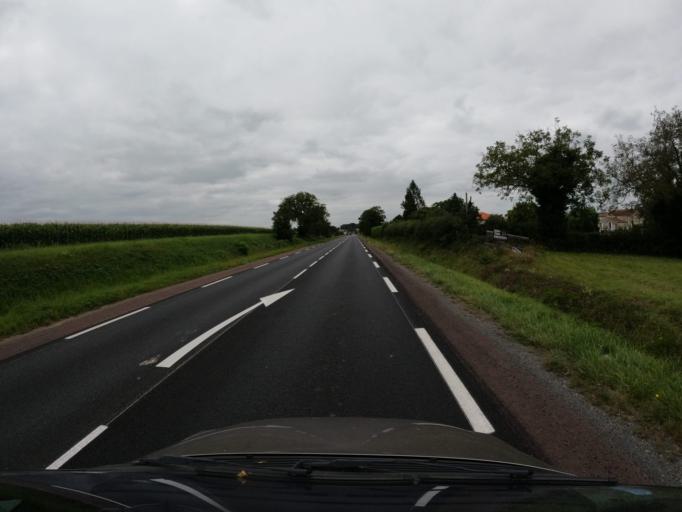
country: FR
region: Pays de la Loire
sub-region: Departement de la Vendee
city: Benet
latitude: 46.3960
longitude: -0.6516
